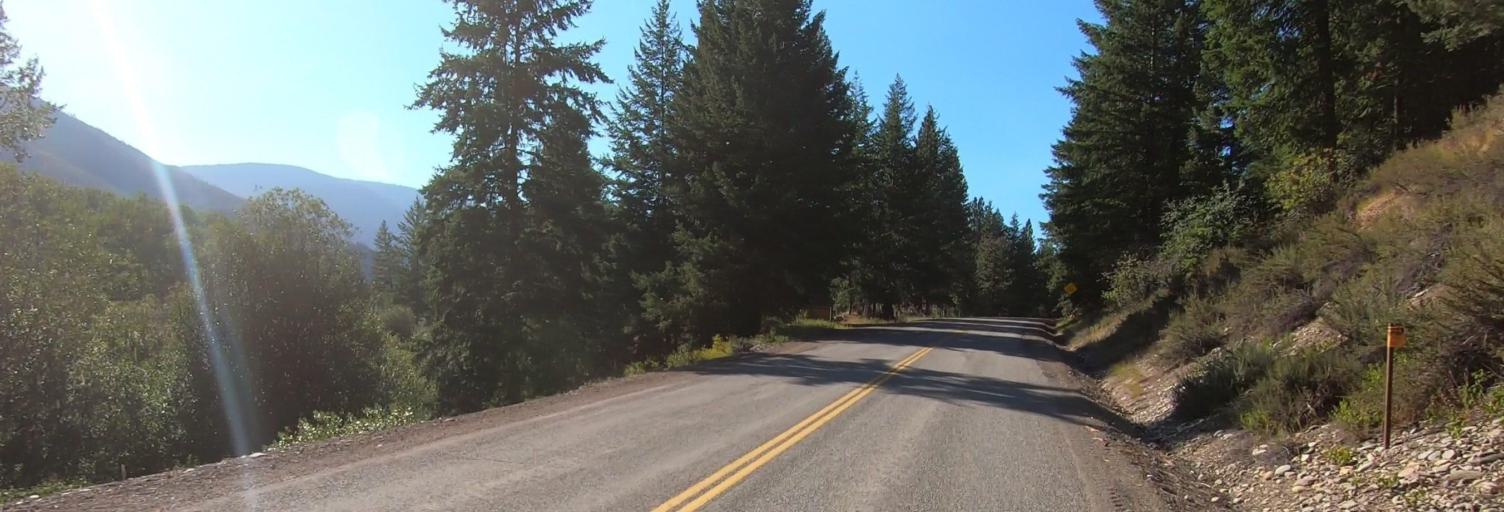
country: US
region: Washington
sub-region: Chelan County
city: Granite Falls
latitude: 48.5596
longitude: -120.3448
